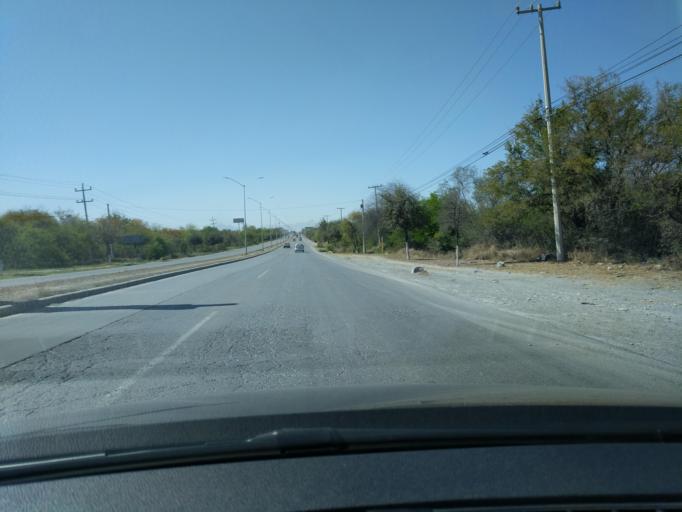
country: MX
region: Nuevo Leon
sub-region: Juarez
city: San Antonio
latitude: 25.6330
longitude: -100.0783
